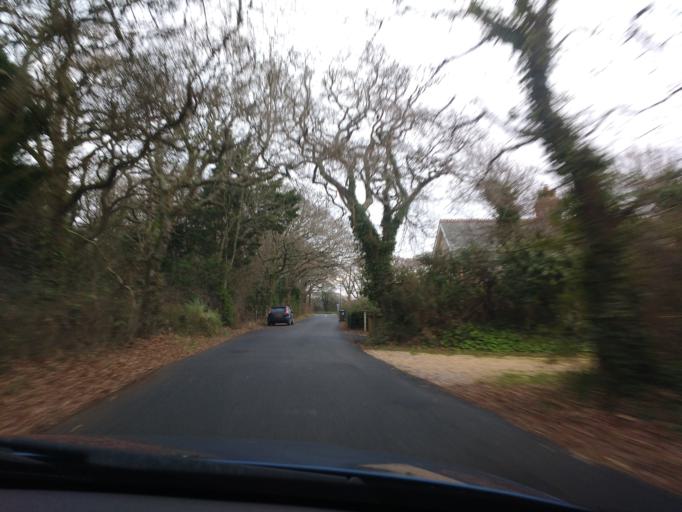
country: GB
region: England
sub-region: Isle of Wight
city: Shalfleet
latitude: 50.7100
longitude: -1.3869
